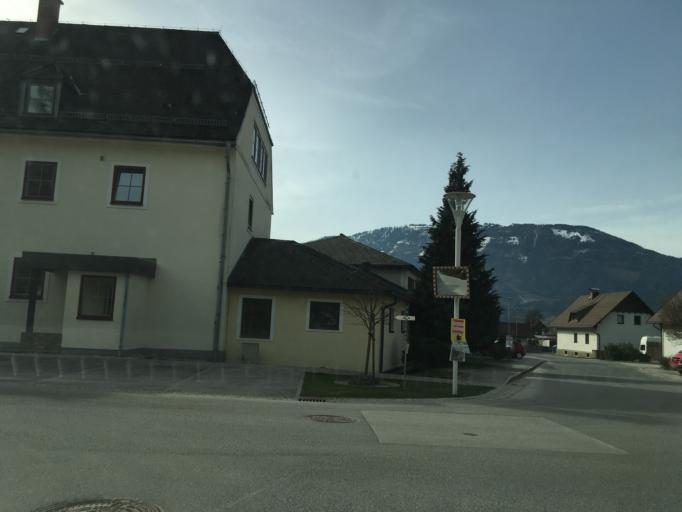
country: AT
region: Styria
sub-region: Politischer Bezirk Liezen
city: Weissenbach bei Liezen
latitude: 47.5713
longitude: 14.2037
